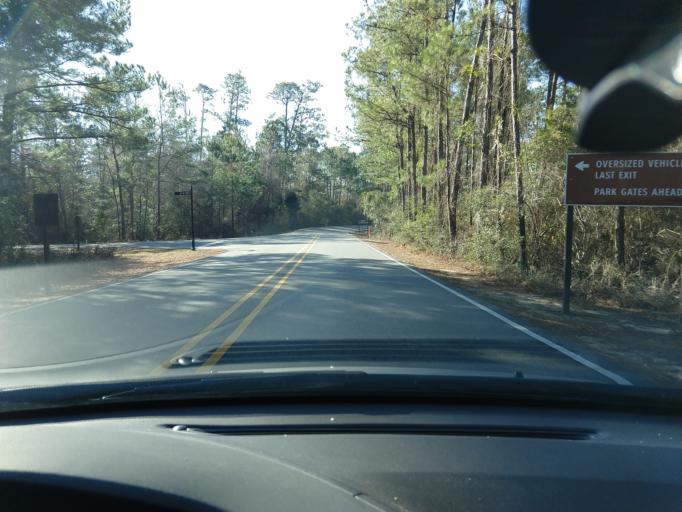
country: US
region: Mississippi
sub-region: Jackson County
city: Gulf Park Estates
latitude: 30.3973
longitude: -88.7783
